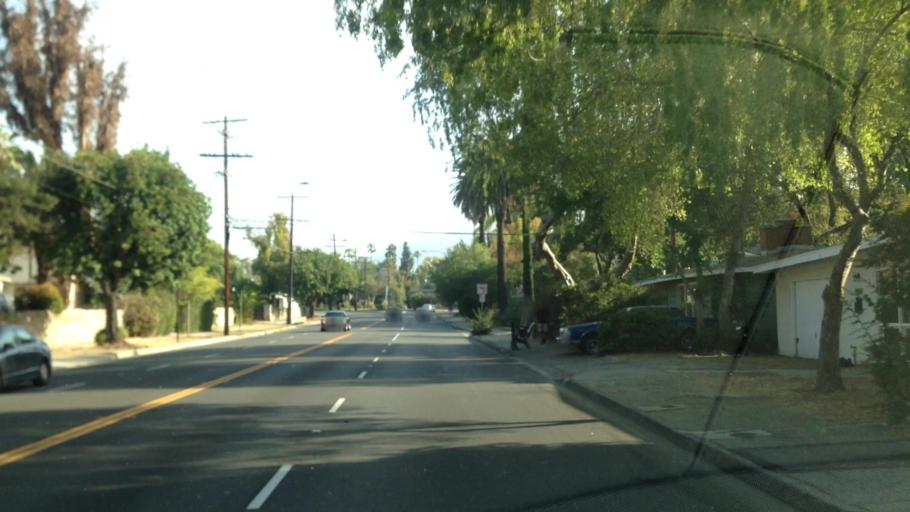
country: US
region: California
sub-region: Los Angeles County
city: South Pasadena
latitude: 34.1293
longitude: -118.1548
